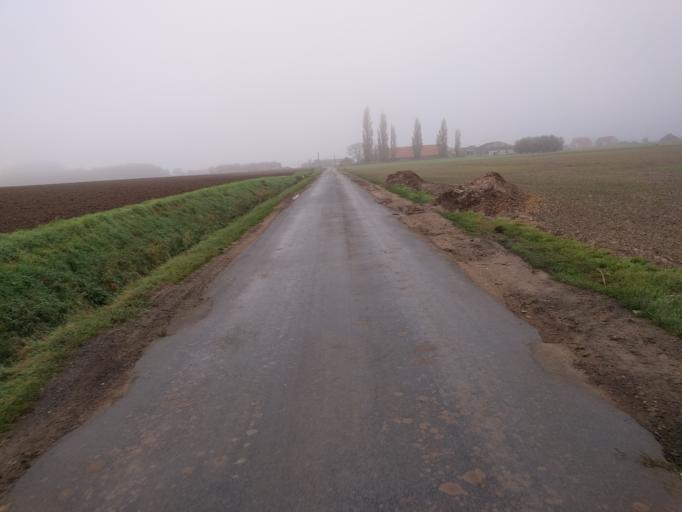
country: BE
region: Flanders
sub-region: Provincie West-Vlaanderen
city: Poperinge
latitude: 50.8230
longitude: 2.7942
